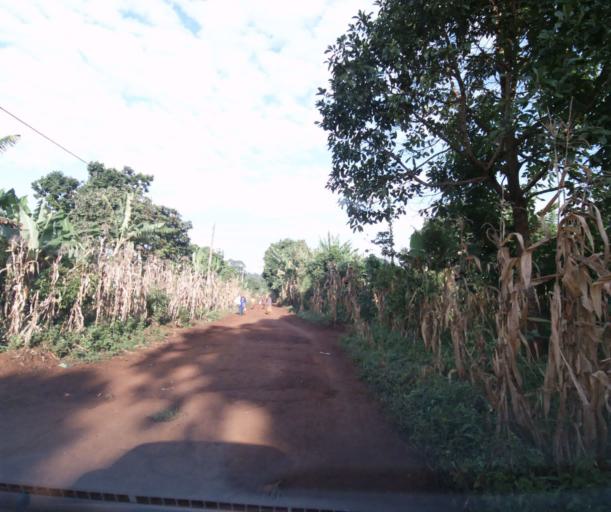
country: CM
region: West
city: Mbouda
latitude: 5.6227
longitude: 10.3428
